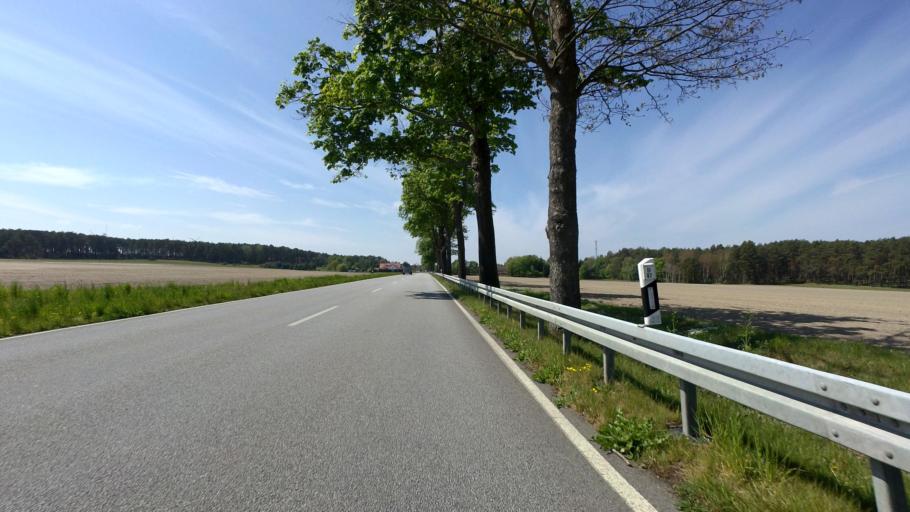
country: DE
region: Brandenburg
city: Schlepzig
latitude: 51.9887
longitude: 13.9896
